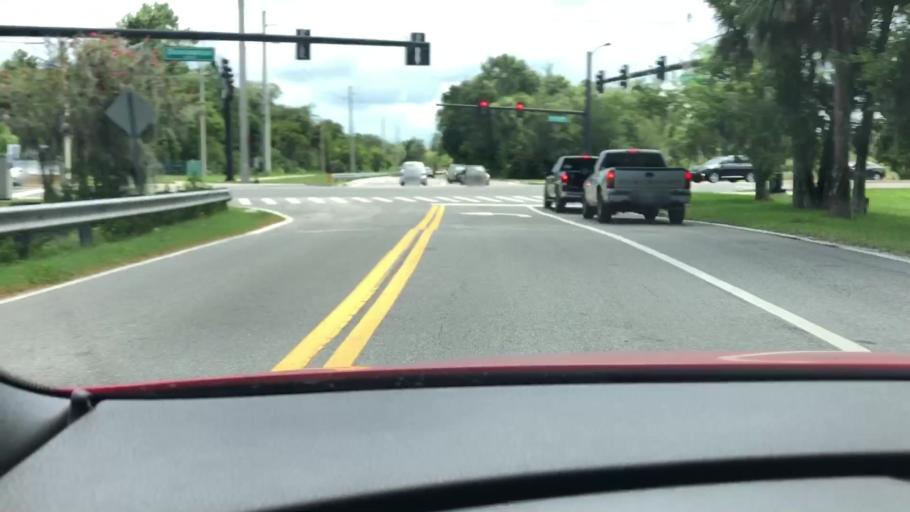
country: US
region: Florida
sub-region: Volusia County
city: Port Orange
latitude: 29.1390
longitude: -80.9975
